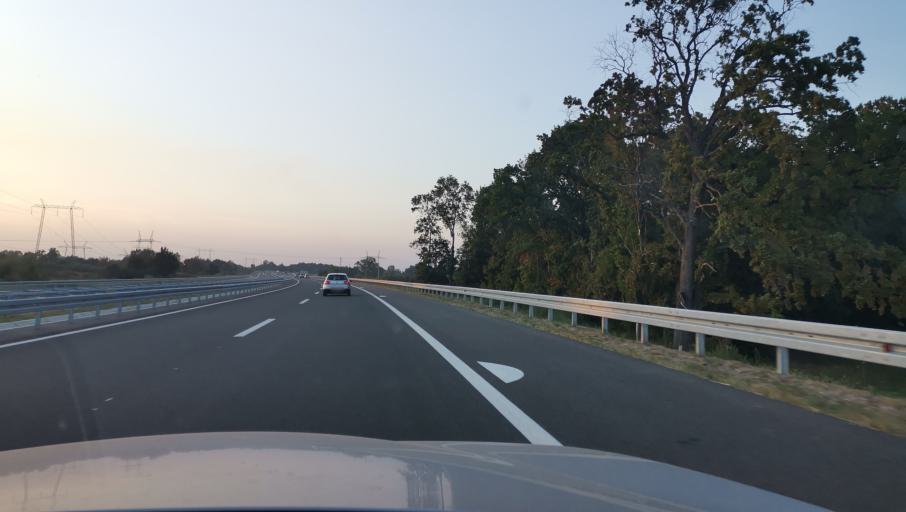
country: RS
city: Zvecka
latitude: 44.6022
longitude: 20.1995
